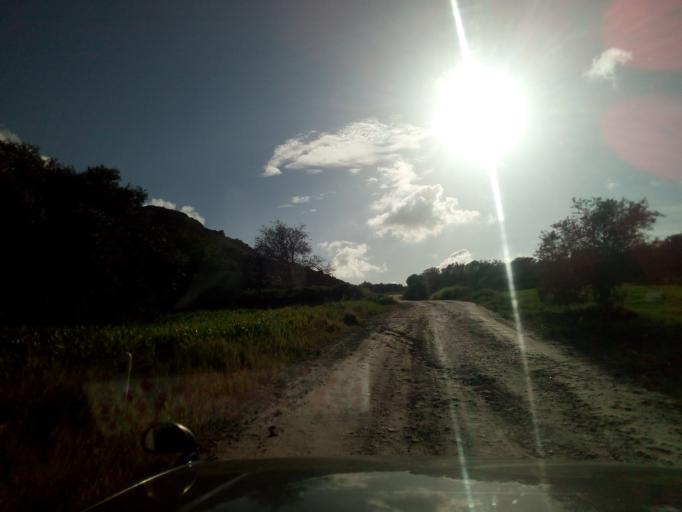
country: CY
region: Larnaka
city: Kofinou
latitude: 34.8048
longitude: 33.4297
